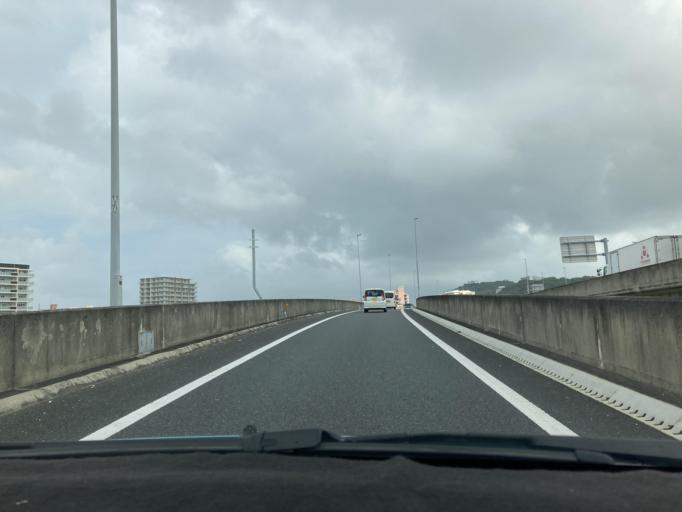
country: JP
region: Okinawa
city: Tomigusuku
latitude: 26.1761
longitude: 127.6705
